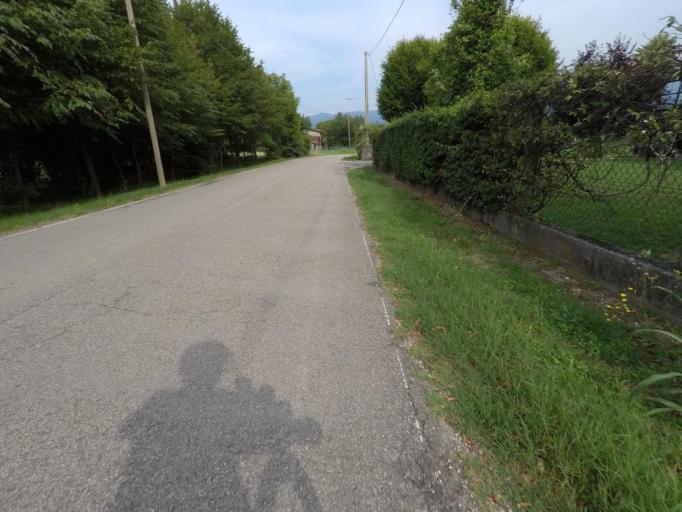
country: IT
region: Veneto
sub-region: Provincia di Treviso
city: Cappella Maggiore
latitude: 45.9654
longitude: 12.3474
